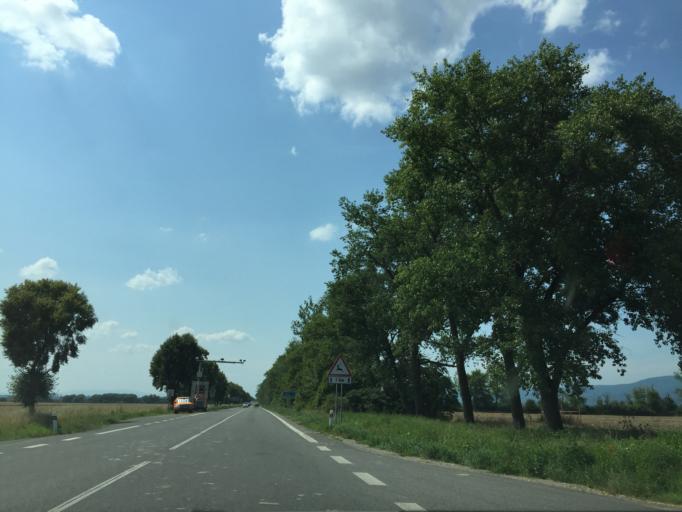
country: SK
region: Kosicky
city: Sobrance
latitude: 48.7608
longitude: 22.1221
